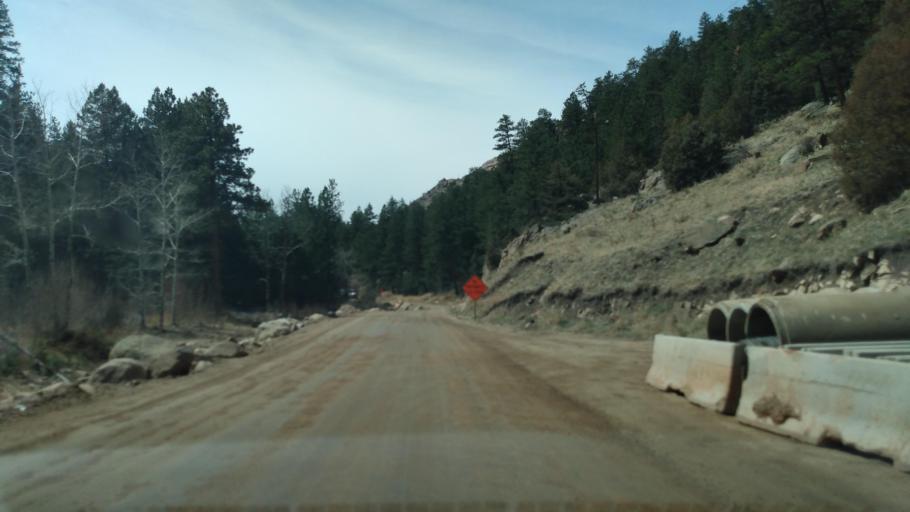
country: US
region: Colorado
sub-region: Boulder County
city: Lyons
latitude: 40.2878
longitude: -105.3776
